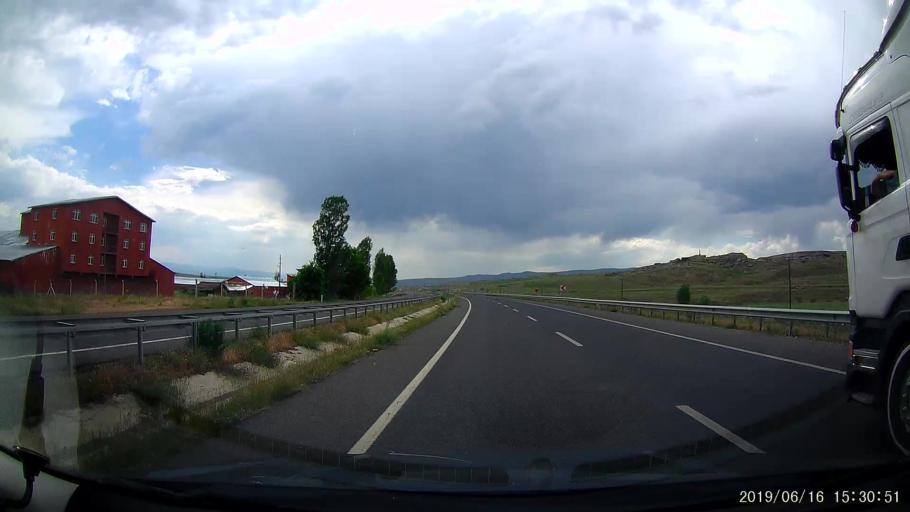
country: TR
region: Erzurum
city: Horasan
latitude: 40.0341
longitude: 42.0936
